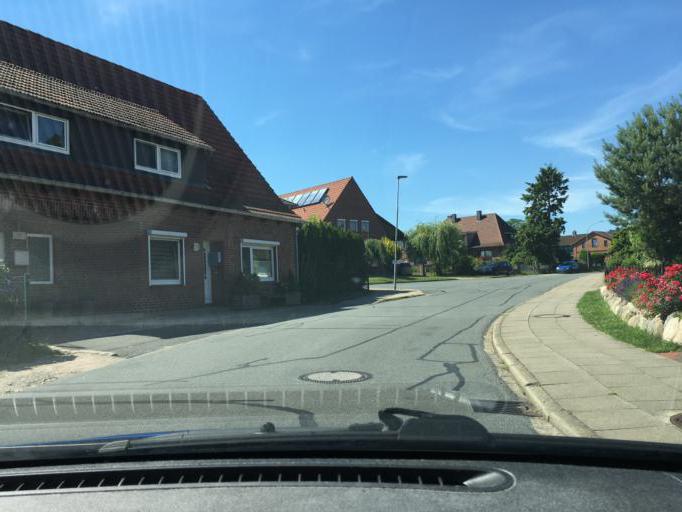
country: DE
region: Lower Saxony
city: Buchholz in der Nordheide
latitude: 53.3804
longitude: 9.8895
